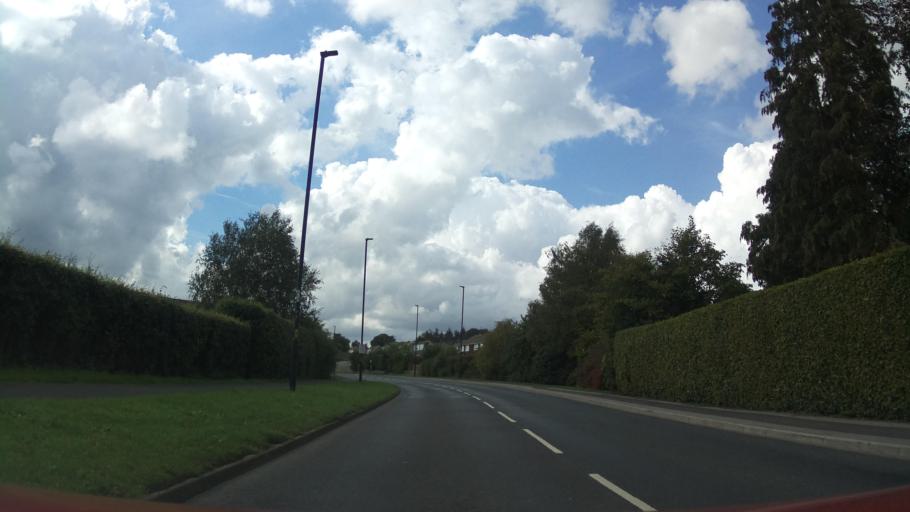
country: GB
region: England
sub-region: North Yorkshire
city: Catterick Garrison
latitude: 54.4110
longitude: -1.7133
